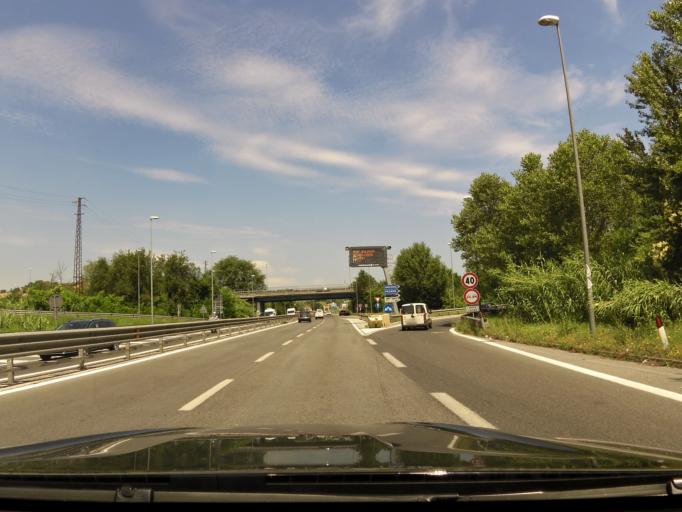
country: IT
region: The Marches
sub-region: Provincia di Ancona
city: San Biagio
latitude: 43.5325
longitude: 13.5151
